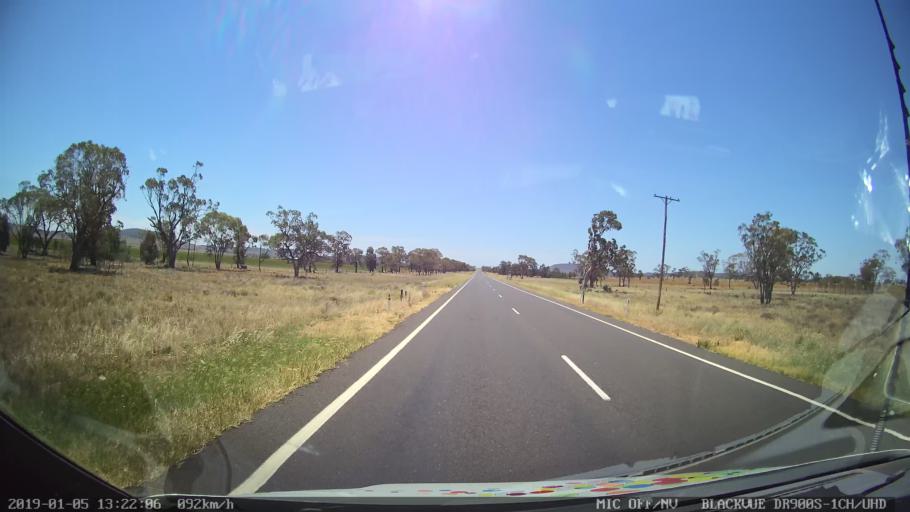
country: AU
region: New South Wales
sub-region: Gunnedah
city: Gunnedah
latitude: -31.0889
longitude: 149.9574
